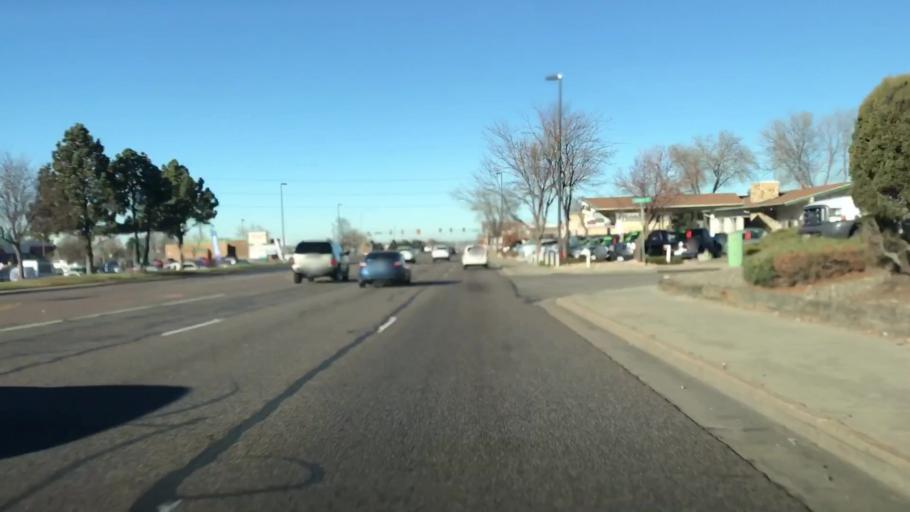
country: US
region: Colorado
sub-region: Adams County
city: Aurora
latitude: 39.6800
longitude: -104.8658
